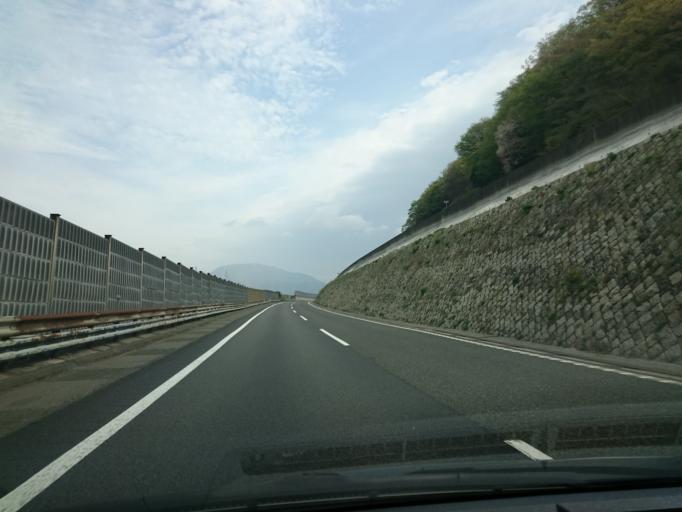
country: JP
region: Shiga Prefecture
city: Nagahama
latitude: 35.3302
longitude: 136.3528
